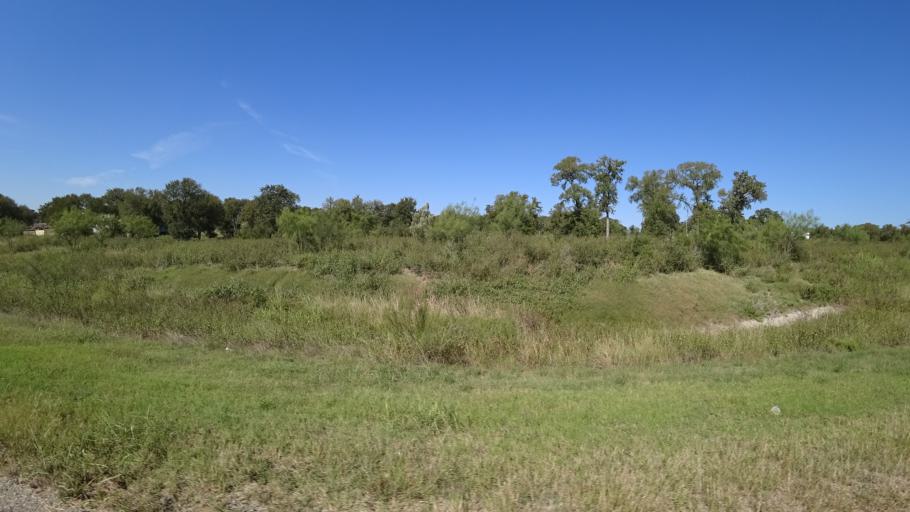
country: US
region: Texas
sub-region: Travis County
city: Hornsby Bend
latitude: 30.2602
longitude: -97.6011
